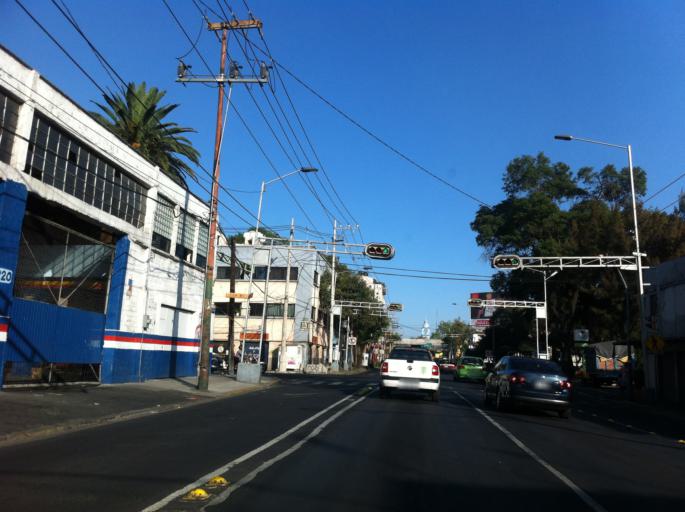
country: MX
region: Mexico City
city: Mexico City
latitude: 19.4134
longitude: -99.1237
